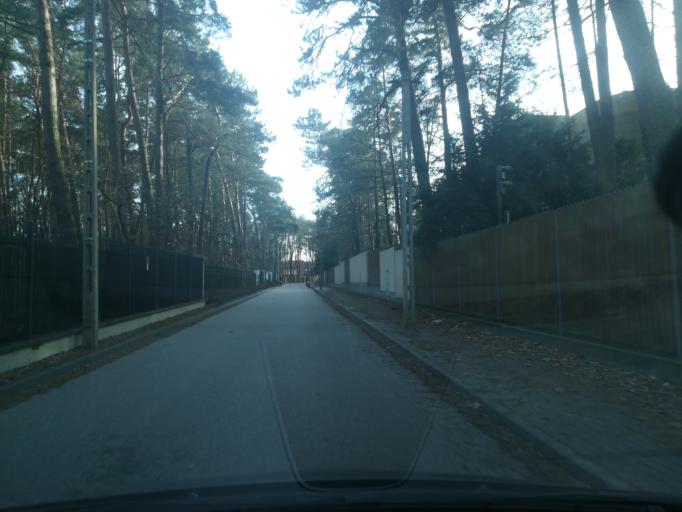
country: PL
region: Masovian Voivodeship
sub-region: Powiat piaseczynski
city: Konstancin-Jeziorna
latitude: 52.0730
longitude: 21.1090
